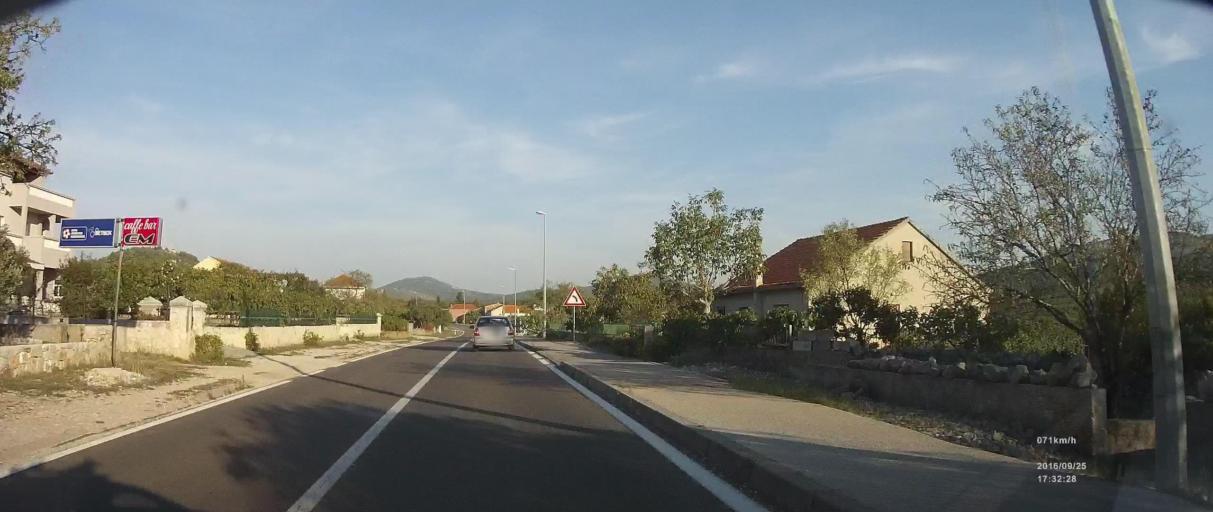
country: HR
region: Sibensko-Kniniska
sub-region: Grad Sibenik
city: Brodarica
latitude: 43.6747
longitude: 16.0029
